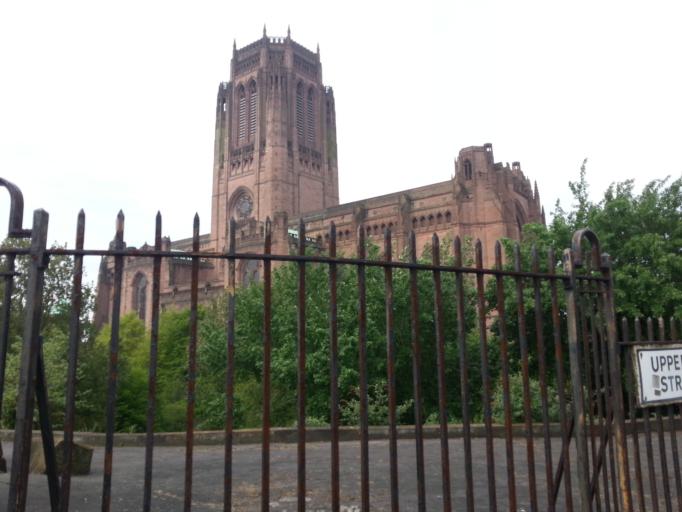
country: GB
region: England
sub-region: Liverpool
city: Liverpool
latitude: 53.3986
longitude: -2.9714
